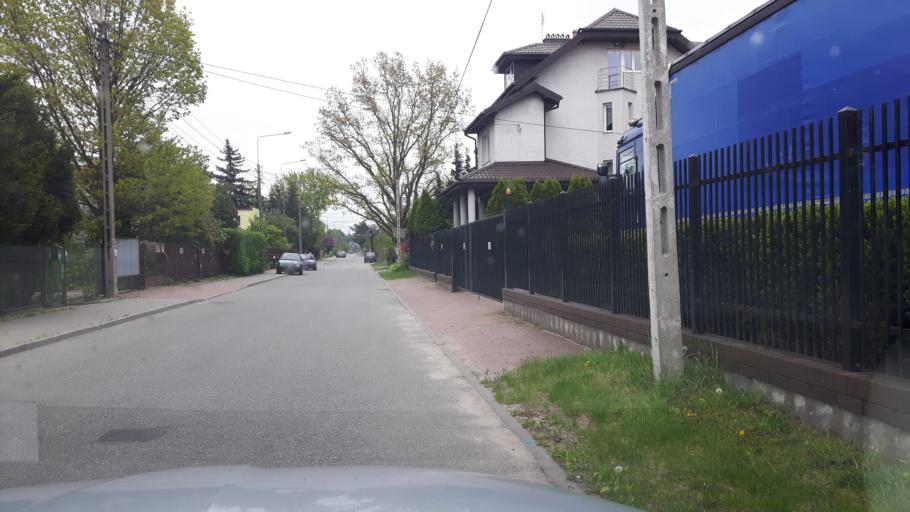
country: PL
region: Masovian Voivodeship
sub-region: Warszawa
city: Rembertow
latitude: 52.2515
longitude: 21.1645
